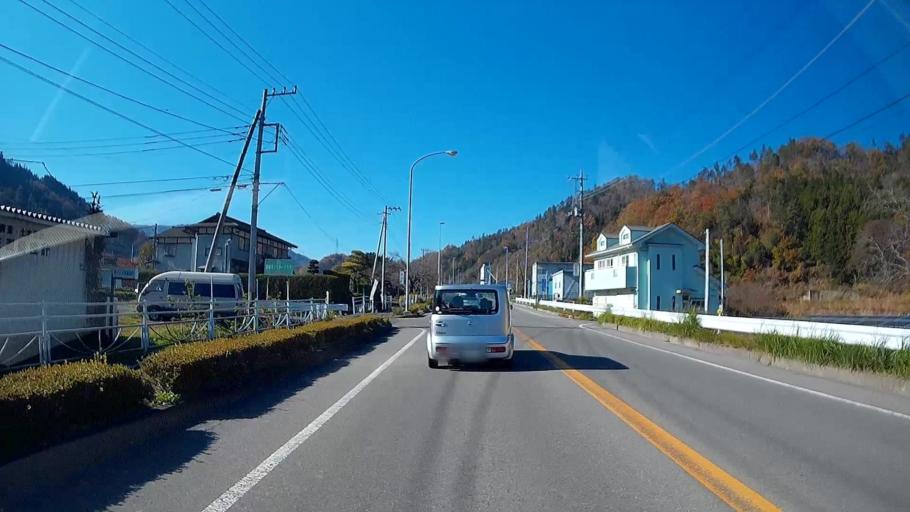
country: JP
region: Yamanashi
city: Otsuki
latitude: 35.5485
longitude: 138.9184
